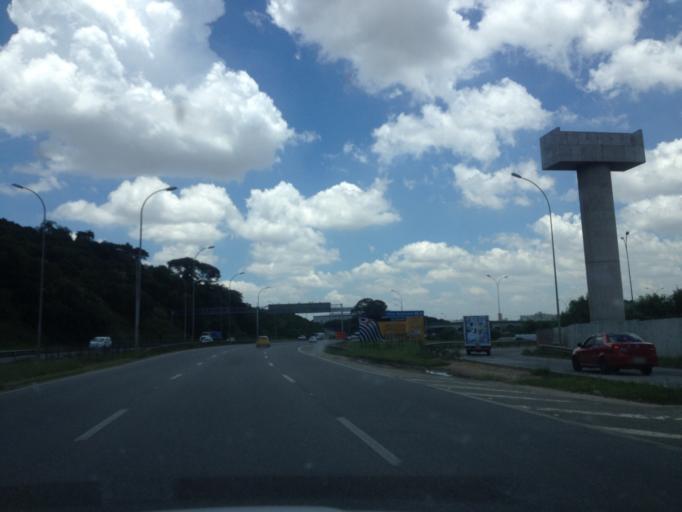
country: BR
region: Sao Paulo
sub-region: Guarulhos
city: Guarulhos
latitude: -23.4533
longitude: -46.4910
